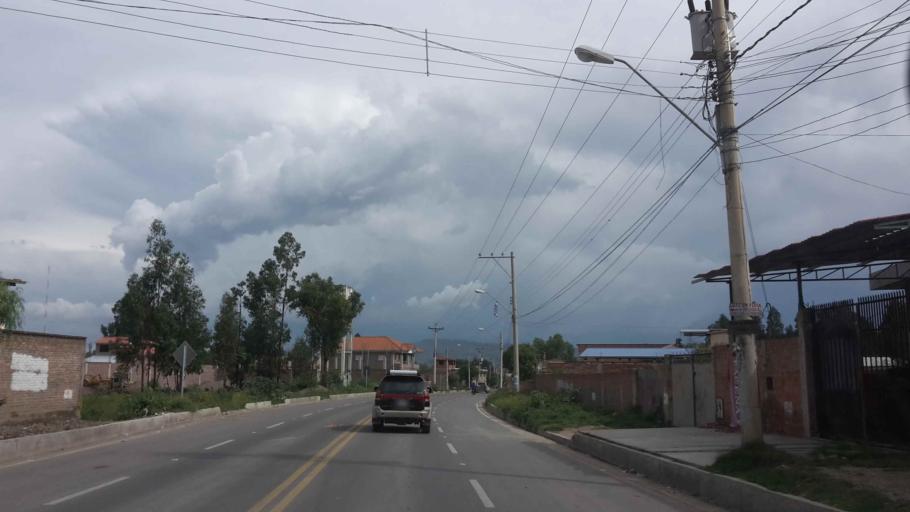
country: BO
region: Cochabamba
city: Cochabamba
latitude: -17.3563
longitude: -66.2543
